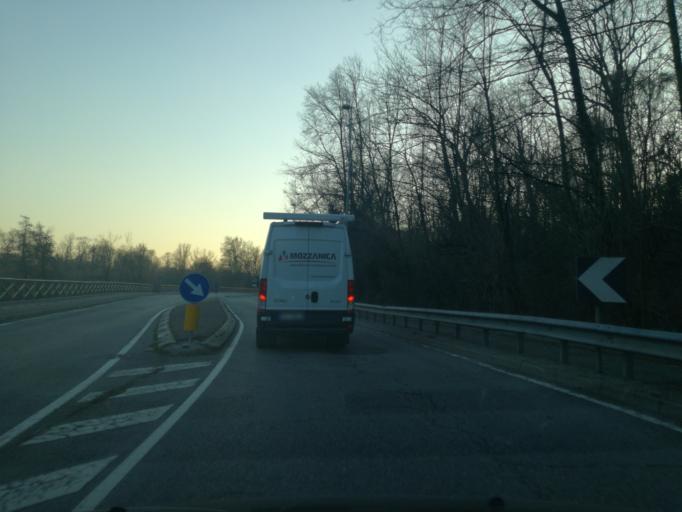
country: IT
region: Lombardy
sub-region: Provincia di Lecco
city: Quattro Strade
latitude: 45.6965
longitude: 9.3856
